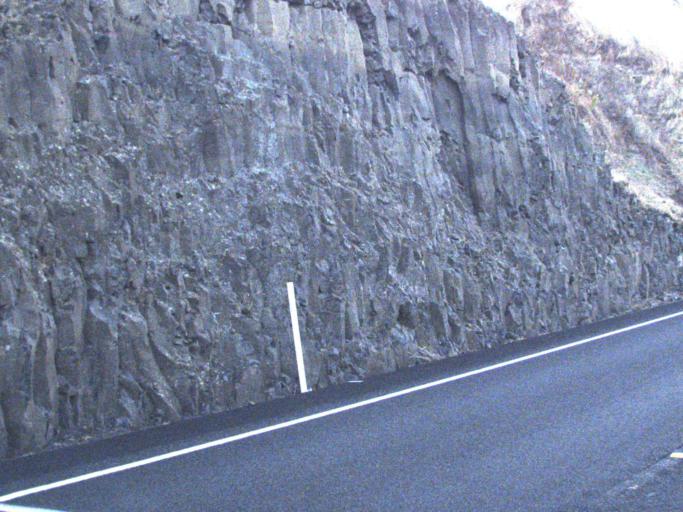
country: US
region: Washington
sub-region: Columbia County
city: Dayton
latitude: 46.5097
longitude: -117.9508
